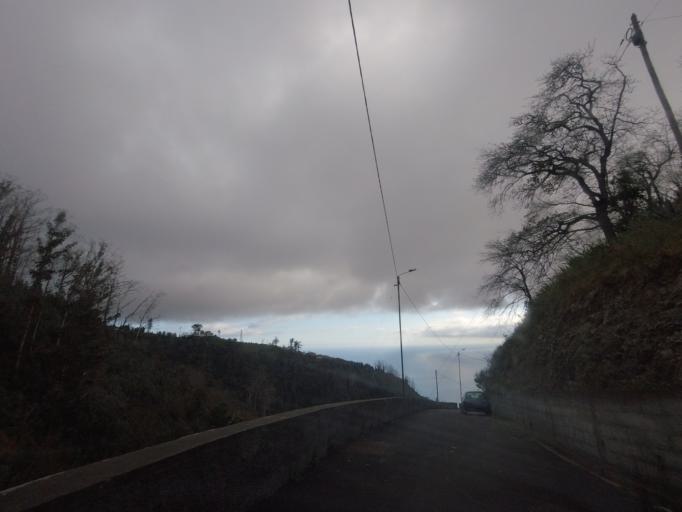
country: PT
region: Madeira
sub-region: Funchal
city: Nossa Senhora do Monte
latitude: 32.6773
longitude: -16.8897
